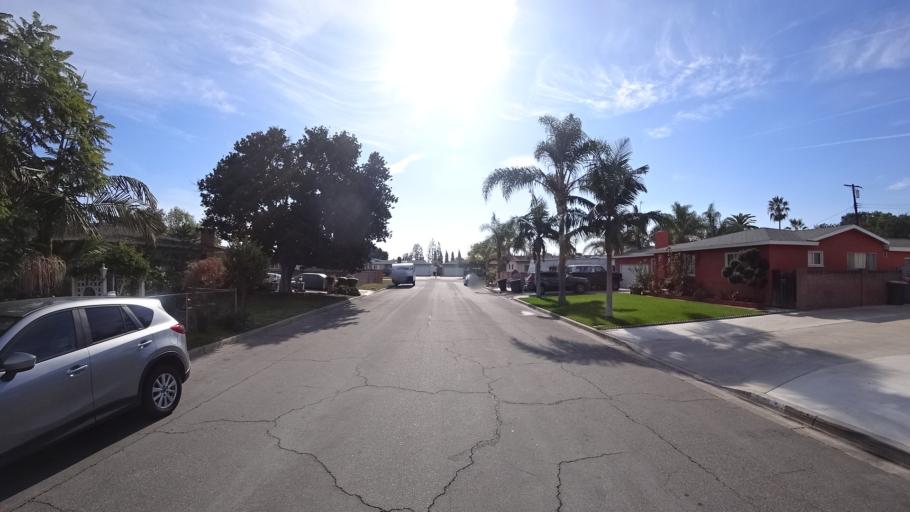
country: US
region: California
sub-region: Orange County
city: Garden Grove
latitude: 33.8004
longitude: -117.9394
